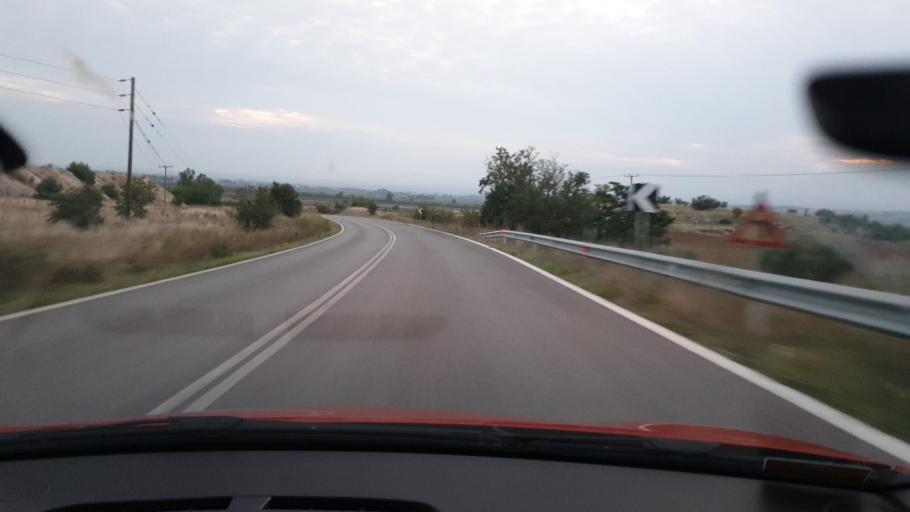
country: GR
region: Central Macedonia
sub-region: Nomos Kilkis
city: Polykastro
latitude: 41.0130
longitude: 22.6392
